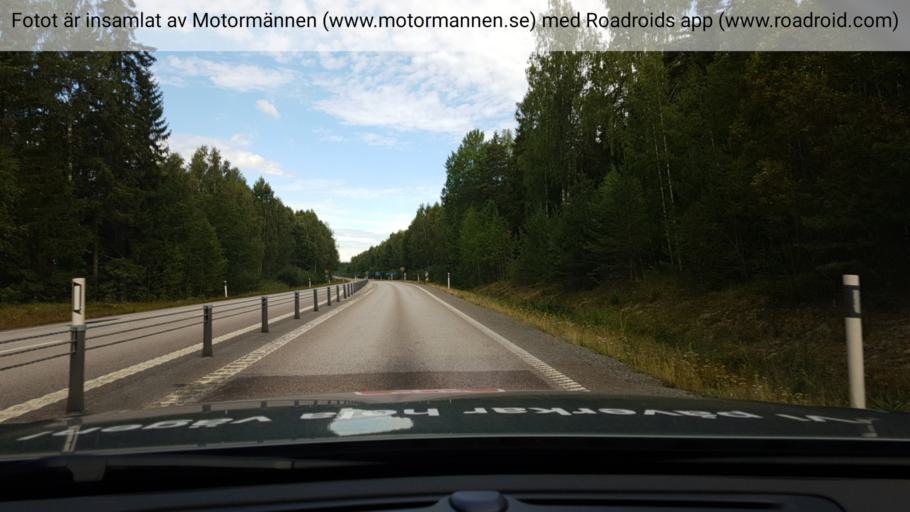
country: SE
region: Uppsala
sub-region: Heby Kommun
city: Tarnsjo
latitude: 60.2846
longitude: 16.9280
